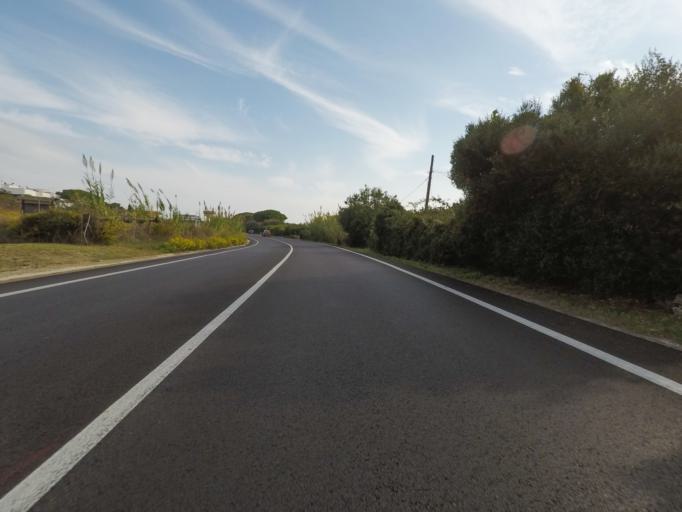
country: IT
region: Latium
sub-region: Citta metropolitana di Roma Capitale
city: Civitavecchia
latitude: 42.0486
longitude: 11.8210
